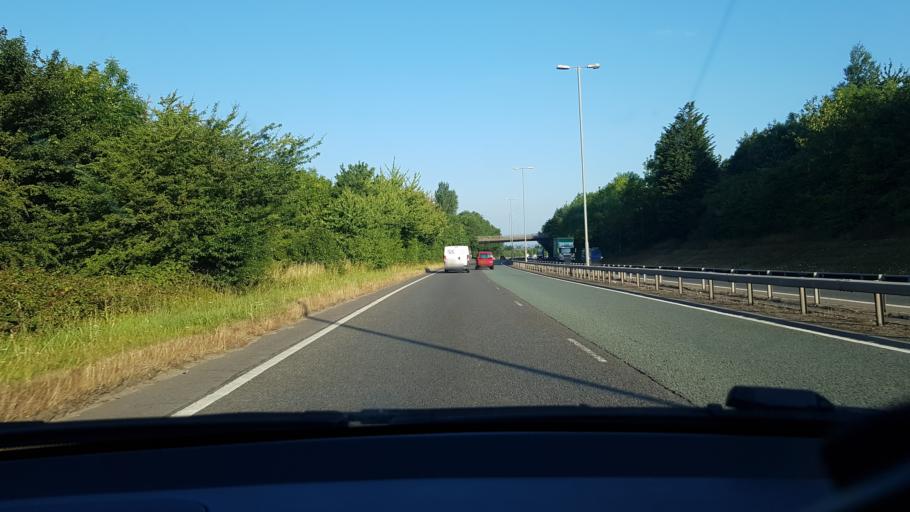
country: GB
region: England
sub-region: Nottinghamshire
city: Eastwood
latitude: 53.0032
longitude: -1.2971
